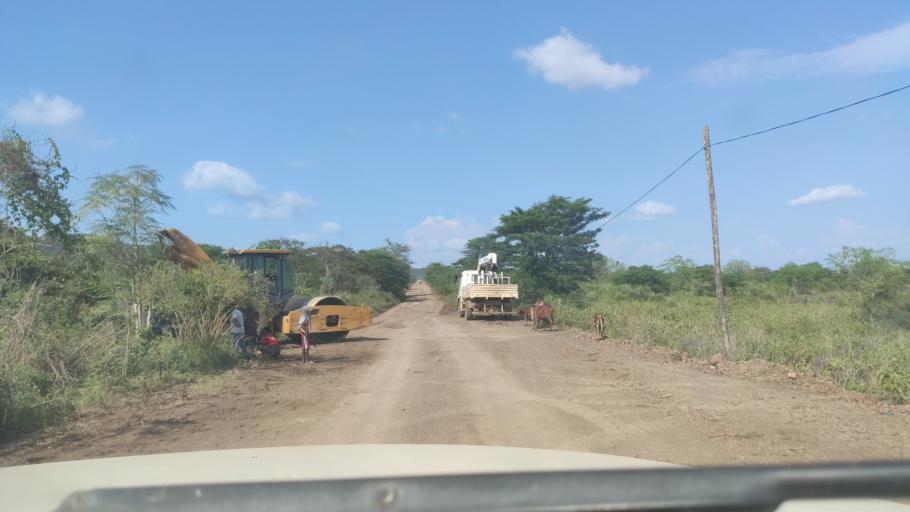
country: ET
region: Southern Nations, Nationalities, and People's Region
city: Felege Neway
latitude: 6.3884
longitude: 37.0971
